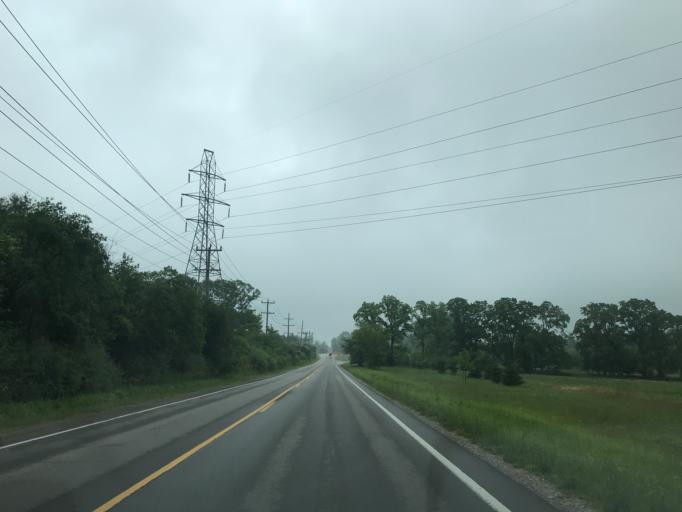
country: US
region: Michigan
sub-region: Washtenaw County
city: Ypsilanti
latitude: 42.2747
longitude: -83.6300
